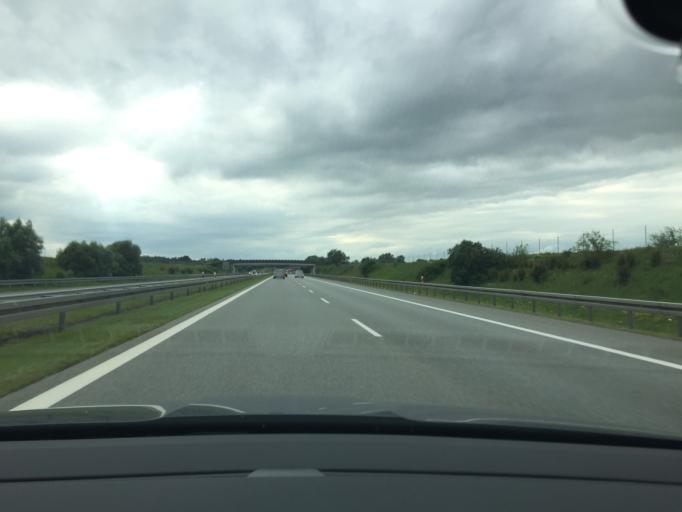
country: PL
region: Greater Poland Voivodeship
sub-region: Powiat poznanski
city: Dopiewo
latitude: 52.3534
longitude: 16.6387
